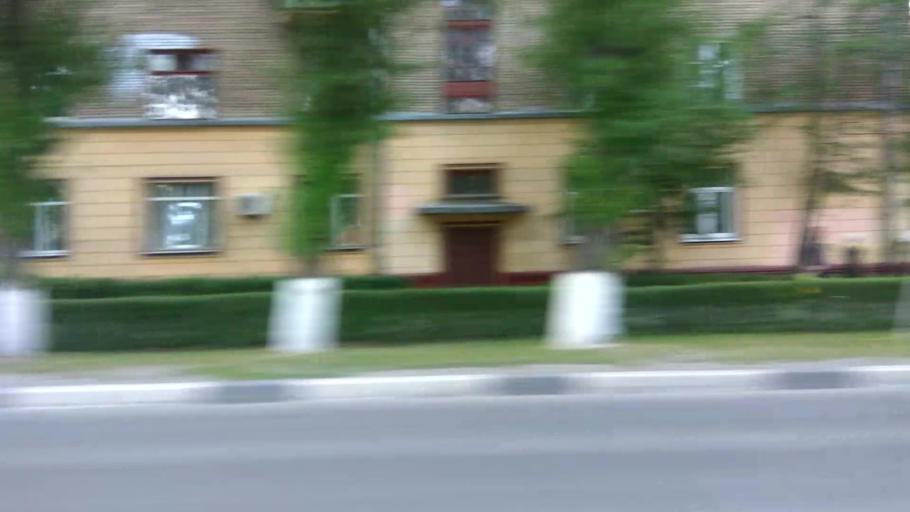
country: RU
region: Moskovskaya
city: Korolev
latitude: 55.9204
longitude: 37.8251
